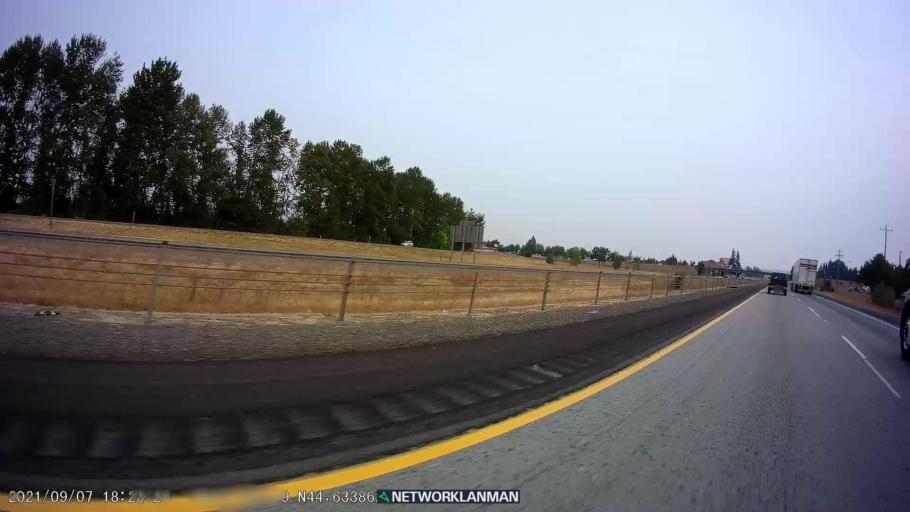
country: US
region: Oregon
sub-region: Linn County
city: Albany
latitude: 44.6337
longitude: -123.0613
